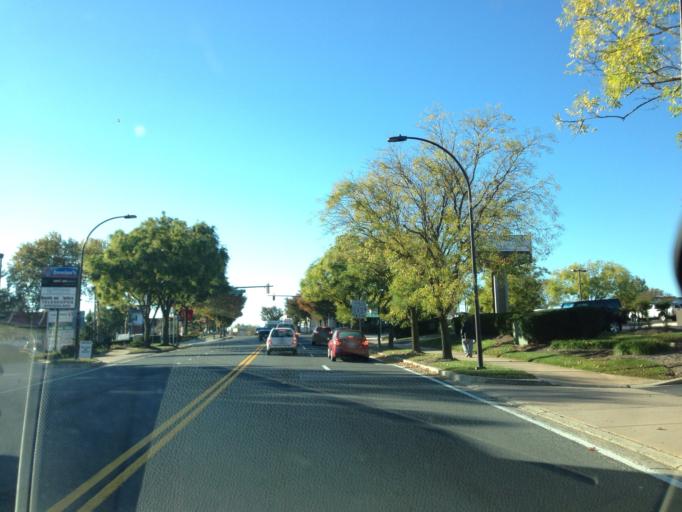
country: US
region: Maryland
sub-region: Montgomery County
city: Damascus
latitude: 39.2911
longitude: -77.2050
